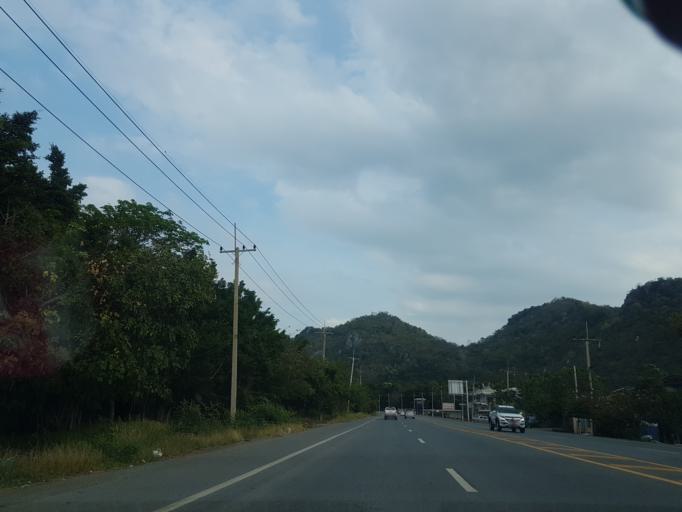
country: TH
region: Sara Buri
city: Phra Phutthabat
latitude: 14.7158
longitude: 100.7894
